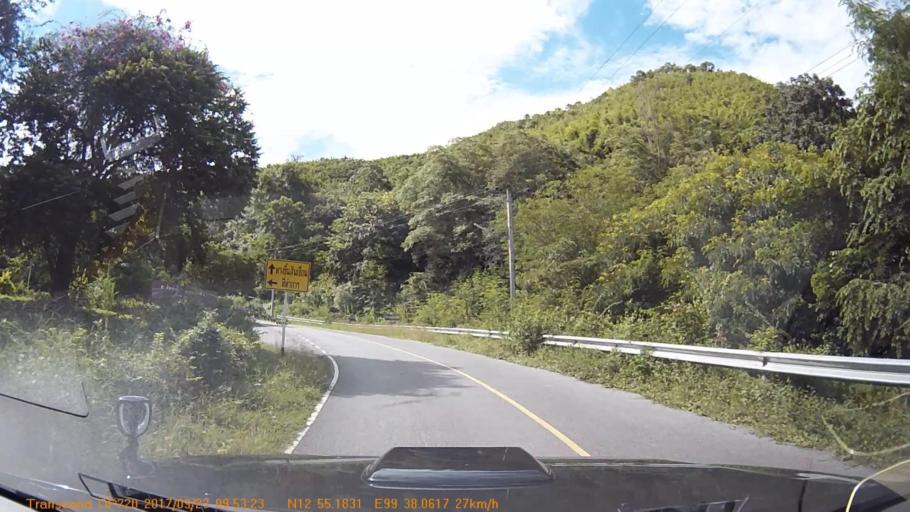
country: TH
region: Phetchaburi
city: Kaeng Krachan
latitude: 12.9196
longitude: 99.6344
